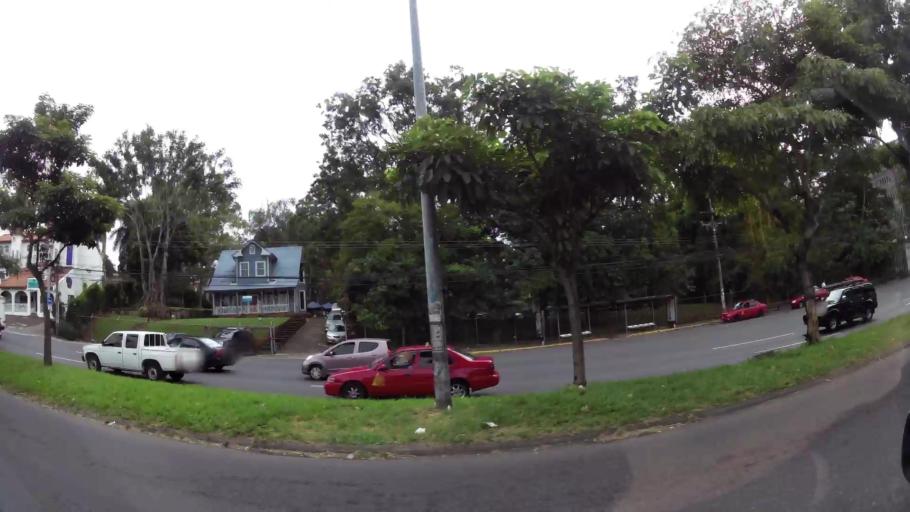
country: CR
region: San Jose
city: San Pedro
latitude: 9.9372
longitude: -84.0543
